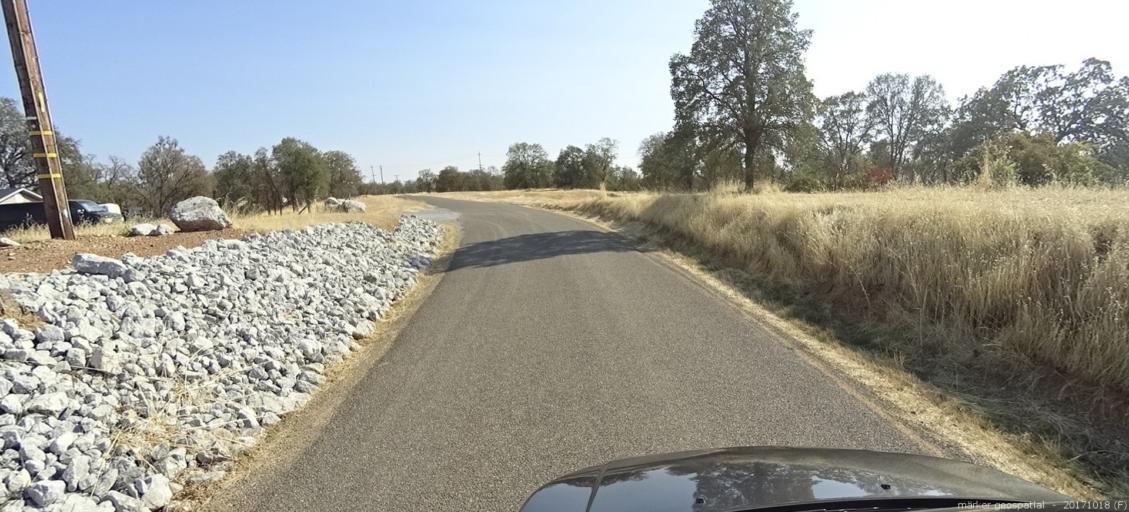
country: US
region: California
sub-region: Shasta County
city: Palo Cedro
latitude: 40.5593
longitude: -122.2568
